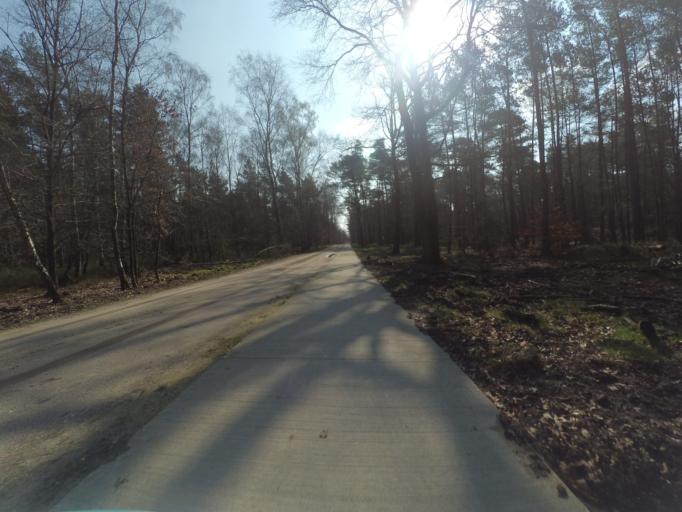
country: NL
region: Gelderland
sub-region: Gemeente Apeldoorn
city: Beekbergen
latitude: 52.1720
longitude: 5.9247
